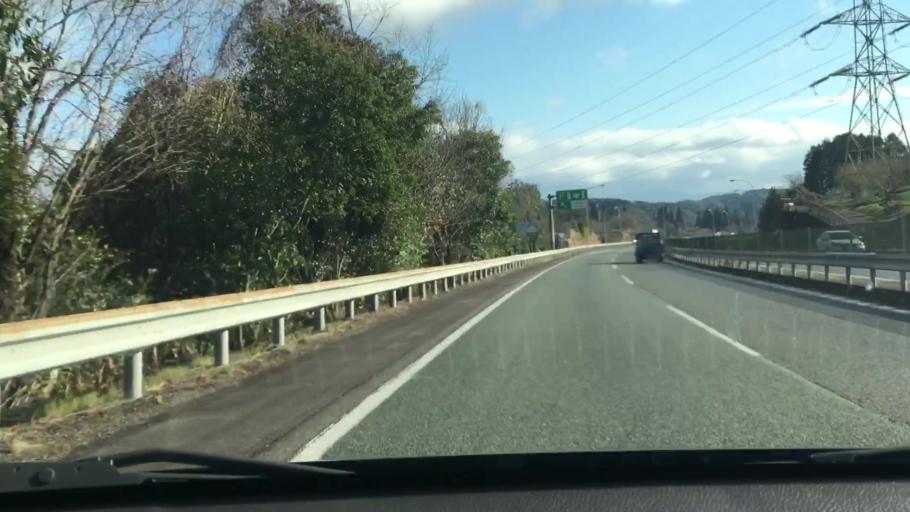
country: JP
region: Kumamoto
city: Hitoyoshi
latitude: 32.2649
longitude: 130.7662
